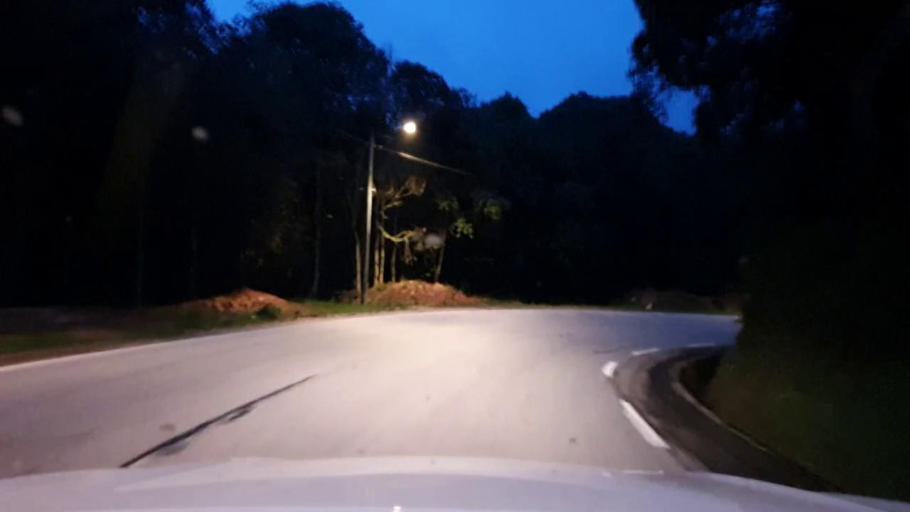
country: RW
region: Southern Province
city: Nzega
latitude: -2.5315
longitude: 29.3903
